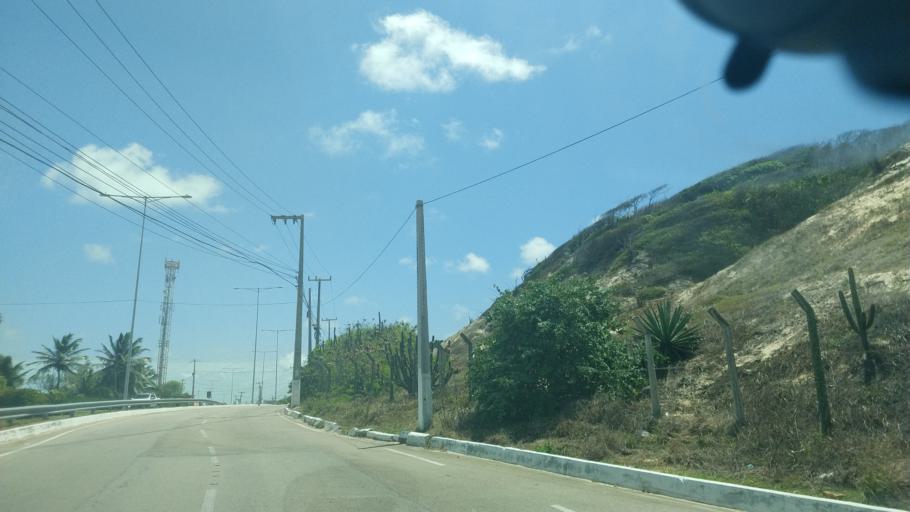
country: BR
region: Rio Grande do Norte
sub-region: Natal
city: Natal
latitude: -5.8270
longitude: -35.1834
